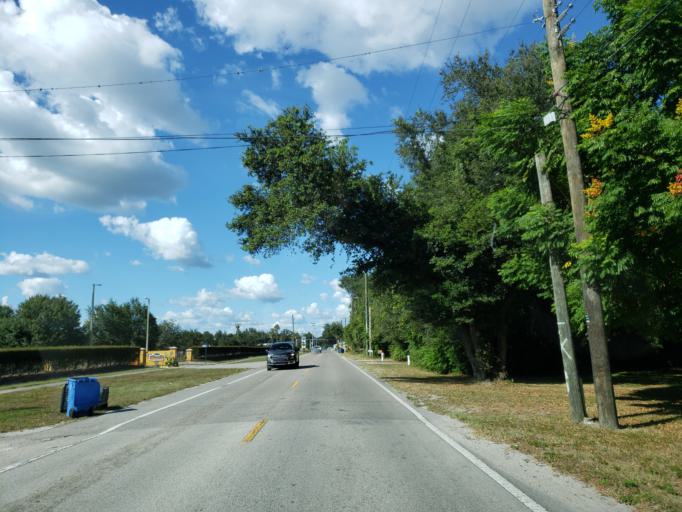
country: US
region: Florida
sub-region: Hillsborough County
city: Dover
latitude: 27.9996
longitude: -82.1869
